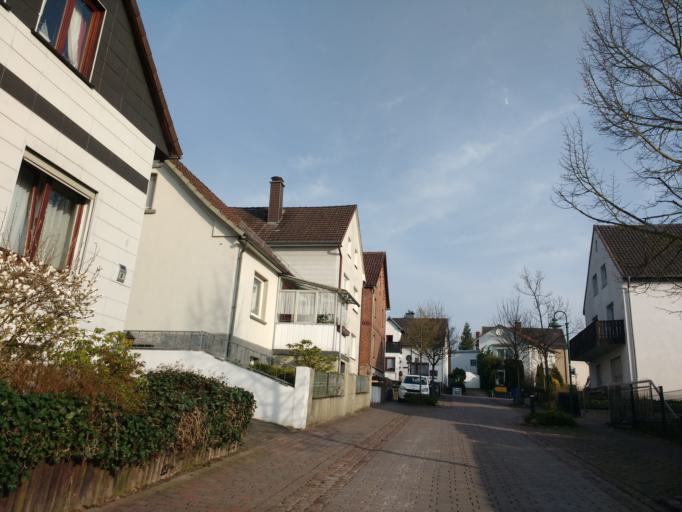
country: DE
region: Lower Saxony
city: Bad Pyrmont
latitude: 51.9857
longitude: 9.2884
